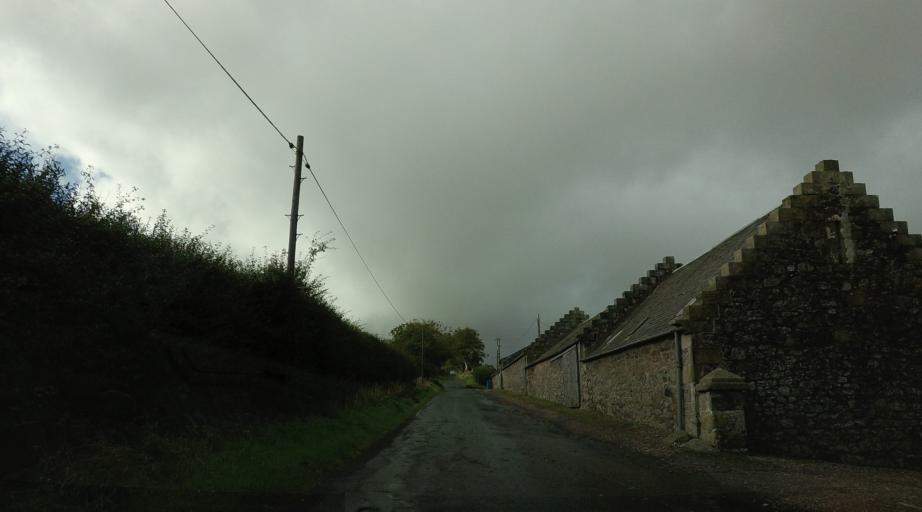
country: GB
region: Scotland
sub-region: Fife
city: Balmullo
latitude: 56.3604
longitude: -2.9509
